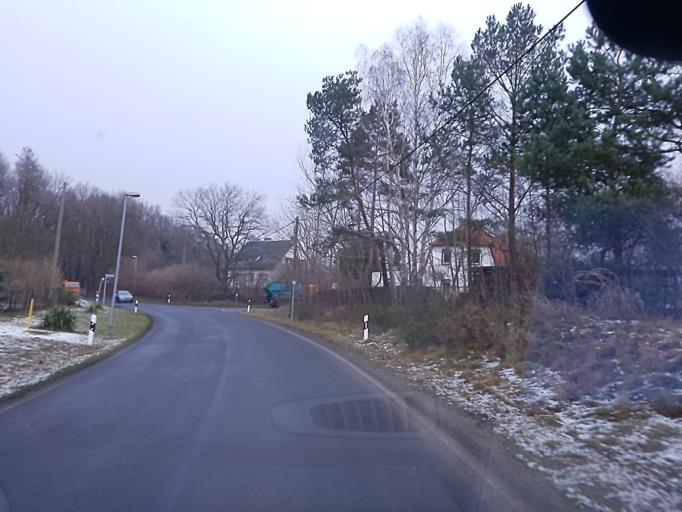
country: DE
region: Brandenburg
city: Lubbenau
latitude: 51.8265
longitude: 13.9191
